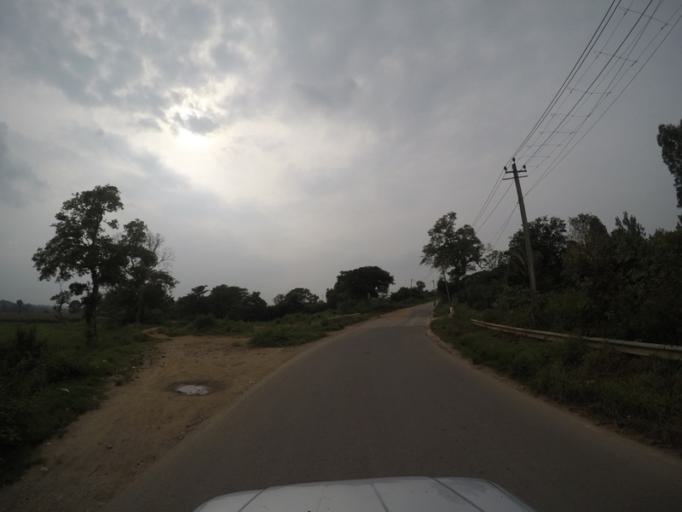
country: IN
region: Karnataka
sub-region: Hassan
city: Belur
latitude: 13.1766
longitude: 75.8719
